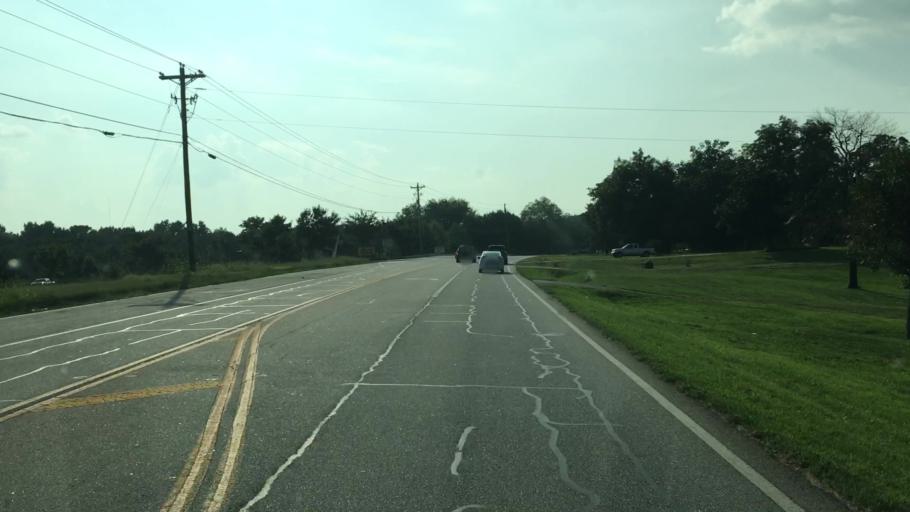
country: US
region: Georgia
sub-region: Jackson County
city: Braselton
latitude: 34.1369
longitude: -83.7883
